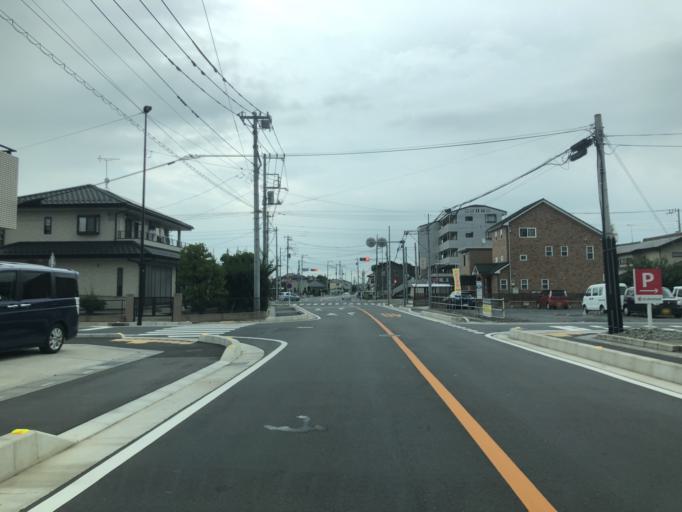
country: JP
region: Saitama
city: Sakado
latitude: 36.0010
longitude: 139.3989
